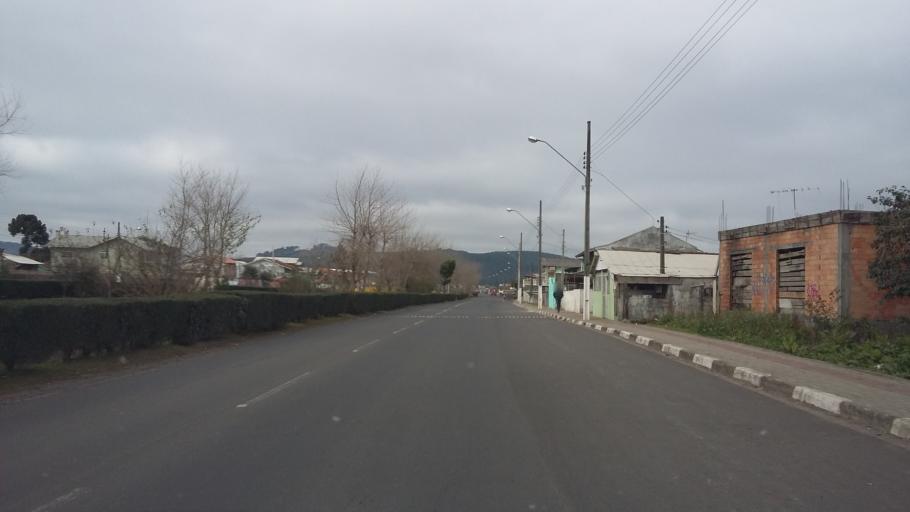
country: BR
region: Santa Catarina
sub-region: Lages
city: Lages
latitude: -27.8250
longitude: -50.3217
